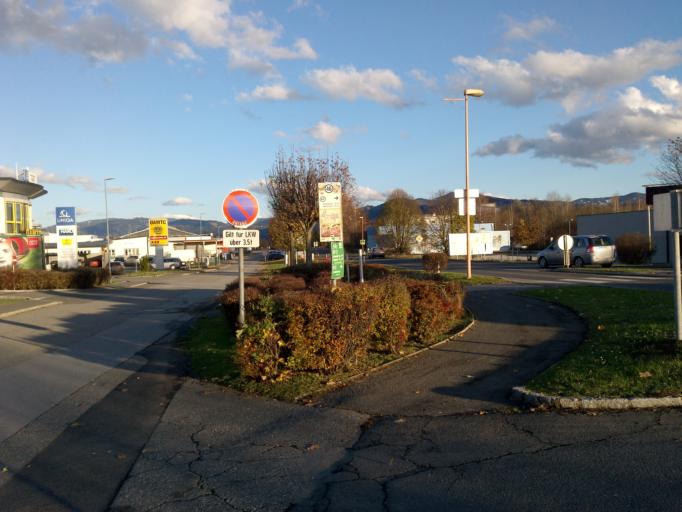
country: AT
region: Styria
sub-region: Politischer Bezirk Murtal
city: Zeltweg
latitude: 47.1946
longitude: 14.7435
